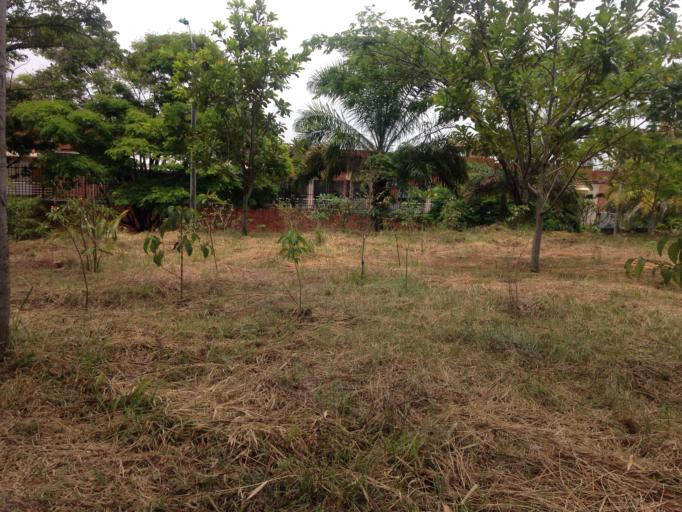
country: CO
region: Valle del Cauca
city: Cali
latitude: 3.3612
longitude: -76.5415
